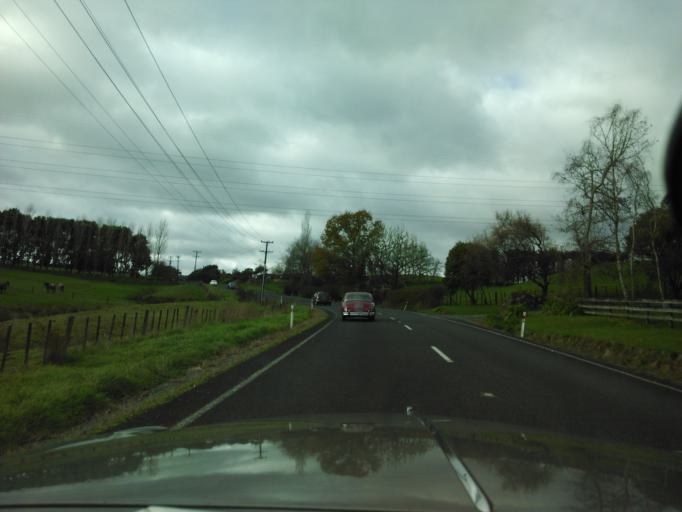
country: NZ
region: Auckland
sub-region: Auckland
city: Red Hill
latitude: -37.1125
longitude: 175.0759
